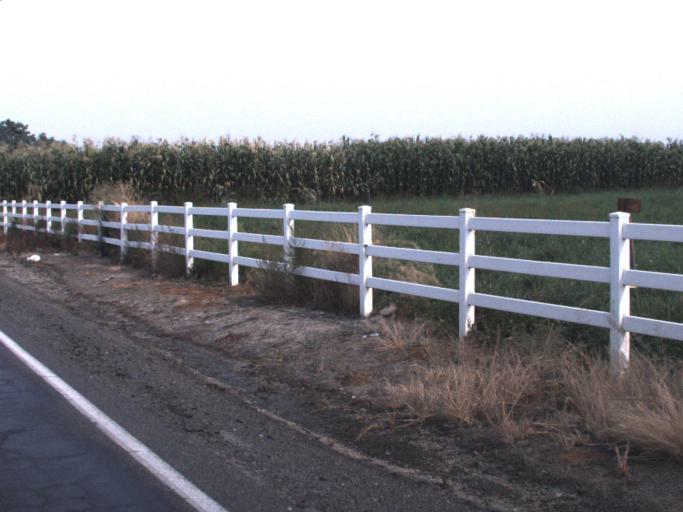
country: US
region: Washington
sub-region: Yakima County
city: Sunnyside
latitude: 46.3355
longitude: -119.9790
